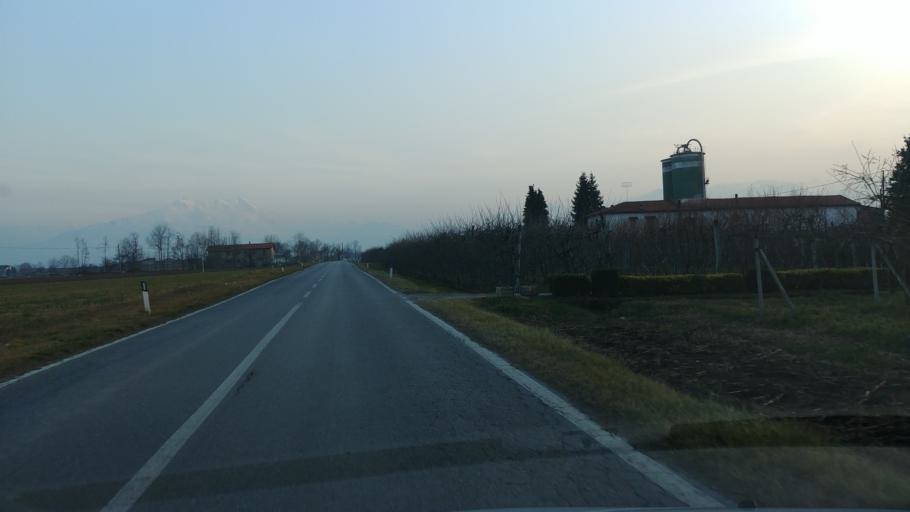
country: IT
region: Piedmont
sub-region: Provincia di Cuneo
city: Roata Rossi
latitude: 44.4229
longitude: 7.5070
